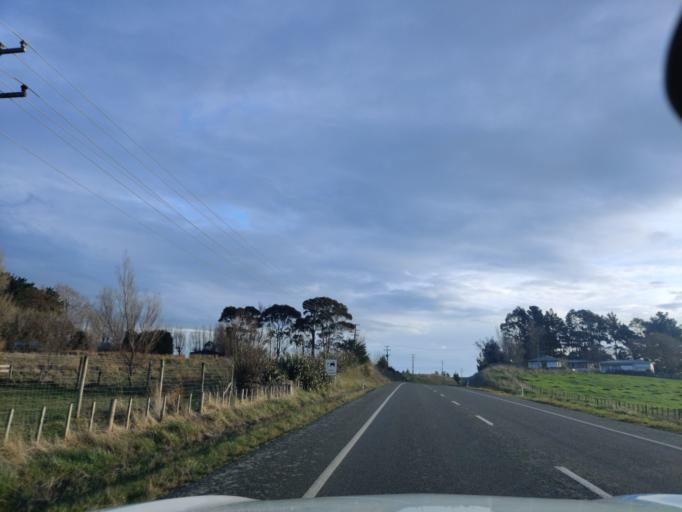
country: NZ
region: Manawatu-Wanganui
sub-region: Palmerston North City
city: Palmerston North
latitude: -40.4047
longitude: 175.6162
